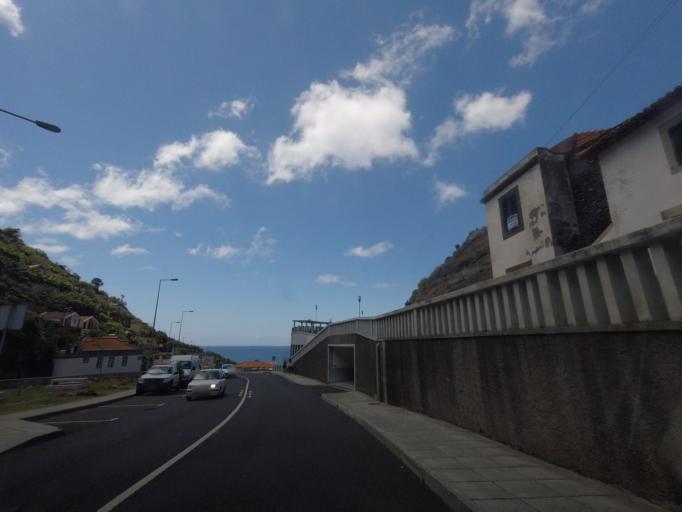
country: PT
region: Madeira
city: Ponta do Sol
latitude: 32.6799
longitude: -17.0772
